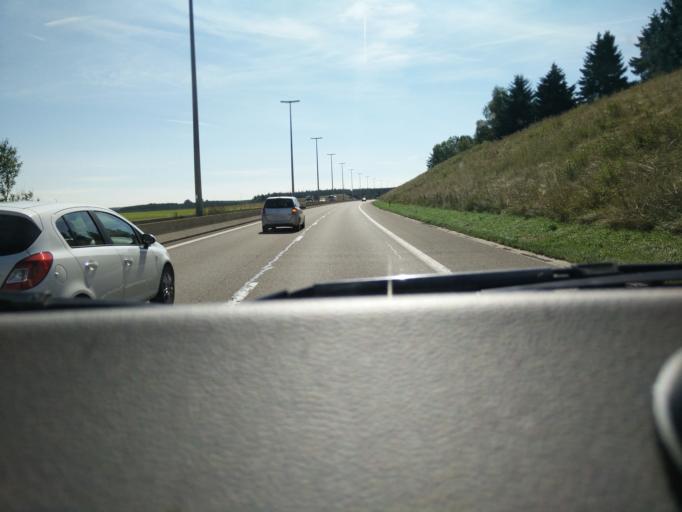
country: BE
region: Wallonia
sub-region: Province du Luxembourg
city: Neufchateau
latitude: 49.8673
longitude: 5.5016
